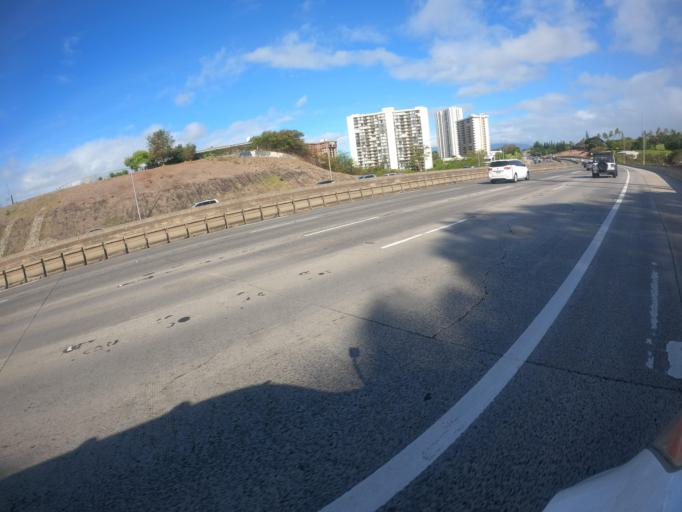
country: US
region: Hawaii
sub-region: Honolulu County
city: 'Aiea
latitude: 21.3850
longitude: -157.9327
